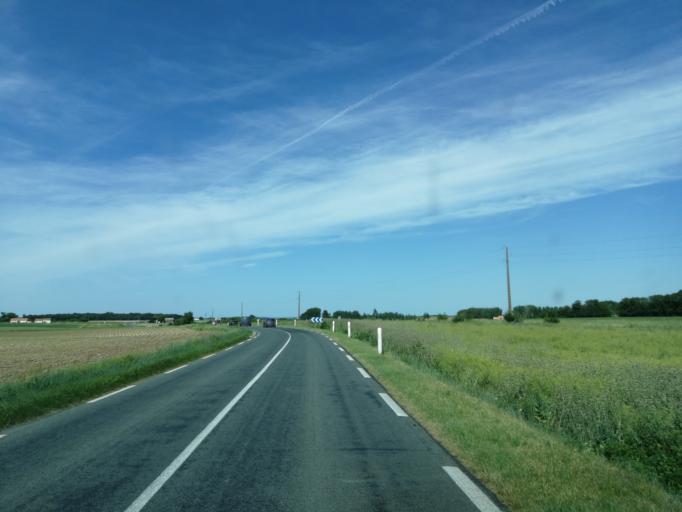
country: FR
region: Poitou-Charentes
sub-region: Departement de la Vienne
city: Loudun
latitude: 47.0298
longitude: 0.1177
